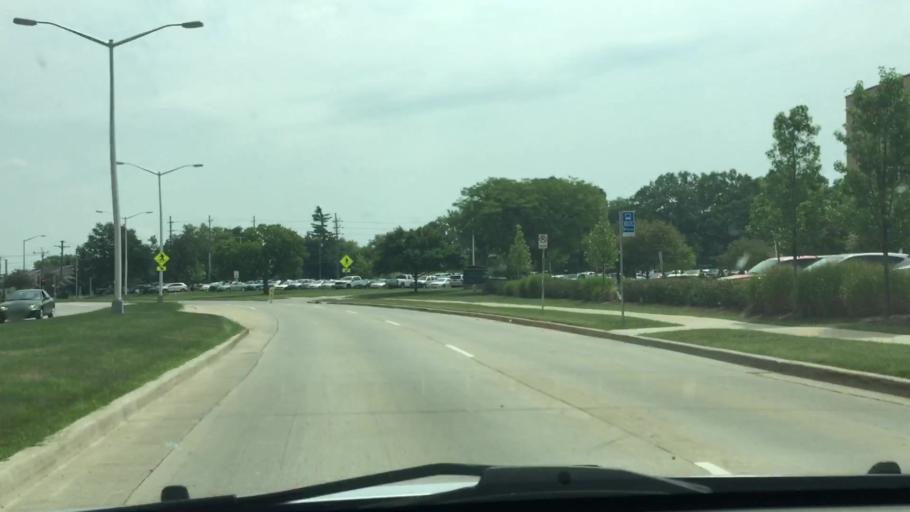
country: US
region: Wisconsin
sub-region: Waukesha County
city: Waukesha
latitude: 43.0235
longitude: -88.2285
